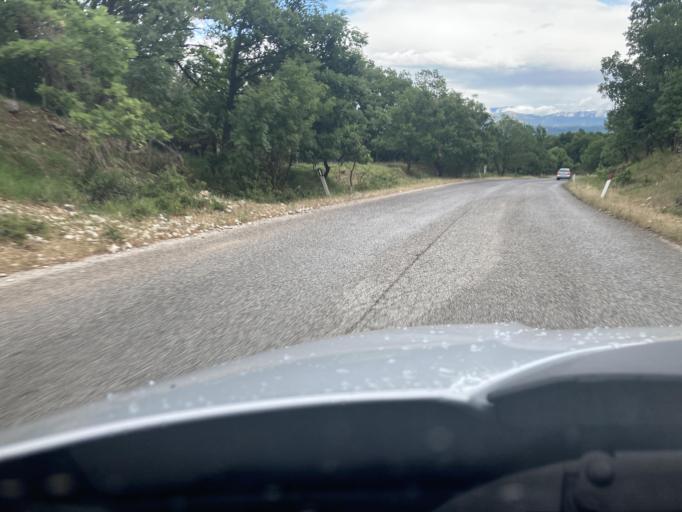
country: IT
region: Abruzzo
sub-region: Provincia dell' Aquila
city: San Panfilo d'Ocre
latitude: 42.2802
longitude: 13.4682
